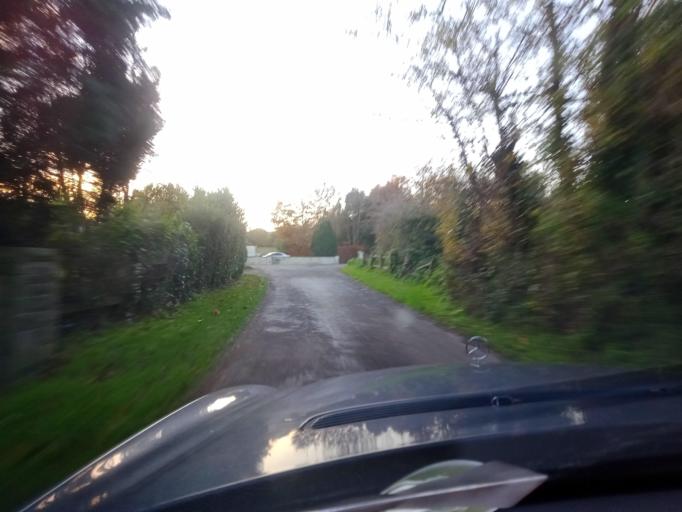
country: IE
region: Leinster
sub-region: Kilkenny
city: Kilkenny
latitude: 52.6105
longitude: -7.1965
